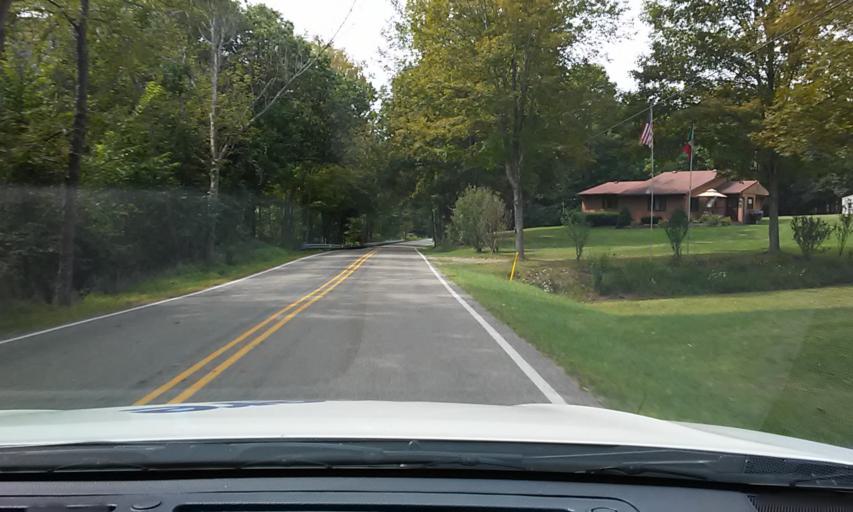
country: US
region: Pennsylvania
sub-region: Cameron County
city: Emporium
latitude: 41.3288
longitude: -78.3368
